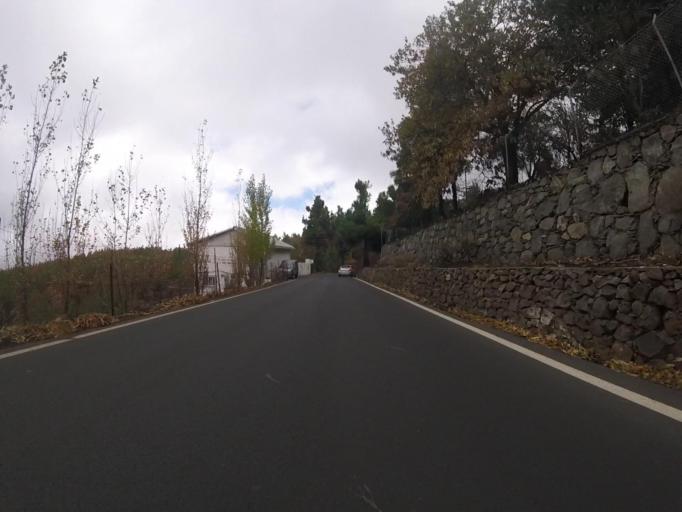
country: ES
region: Canary Islands
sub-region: Provincia de Las Palmas
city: San Bartolome
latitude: 27.9665
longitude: -15.5656
